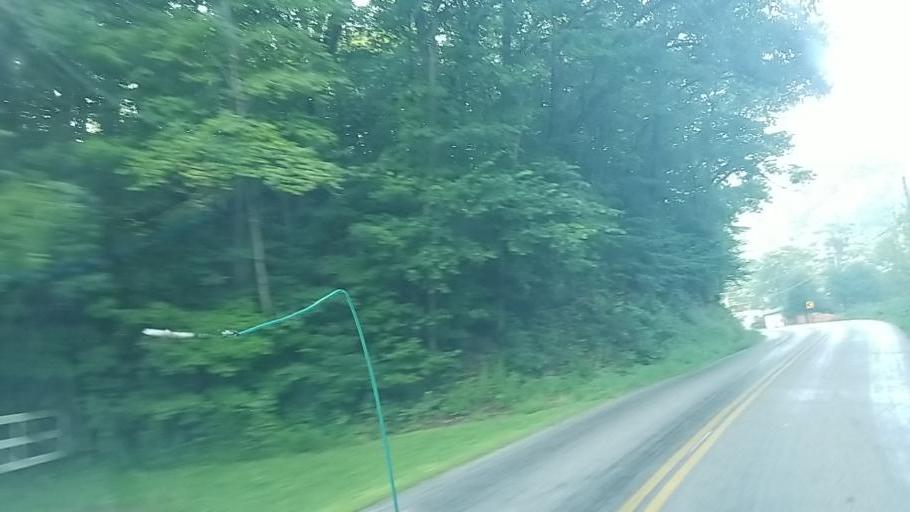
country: US
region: Ohio
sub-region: Wayne County
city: Wooster
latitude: 40.8684
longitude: -82.0186
